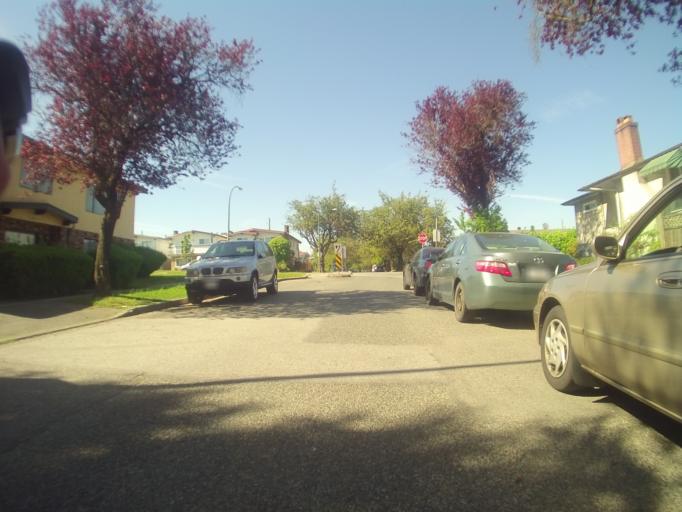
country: CA
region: British Columbia
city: Vancouver
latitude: 49.2178
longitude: -123.0800
